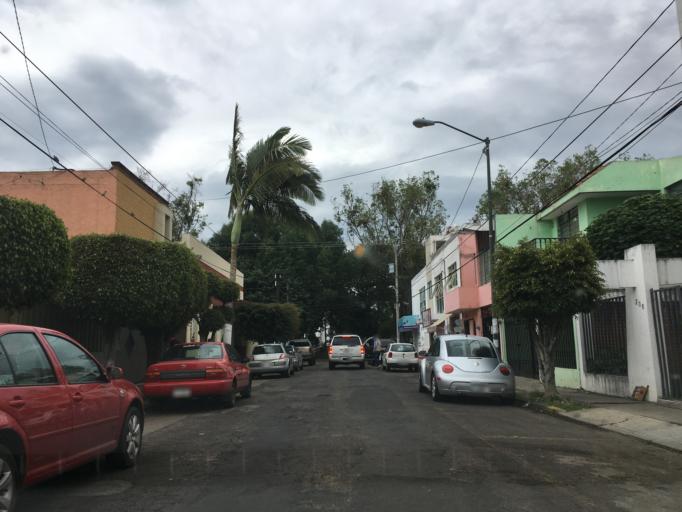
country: MX
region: Michoacan
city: Morelia
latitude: 19.6915
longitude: -101.1753
